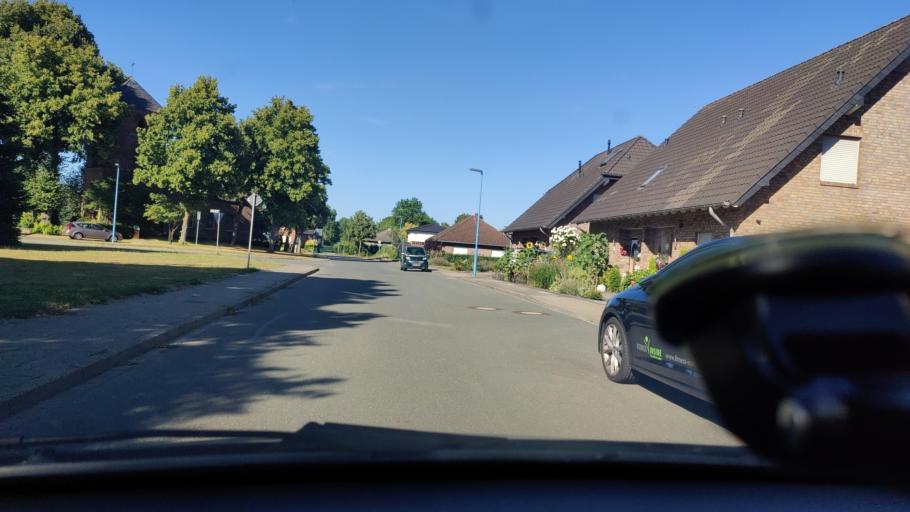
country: DE
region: North Rhine-Westphalia
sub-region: Regierungsbezirk Dusseldorf
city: Kleve
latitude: 51.7706
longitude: 6.2026
